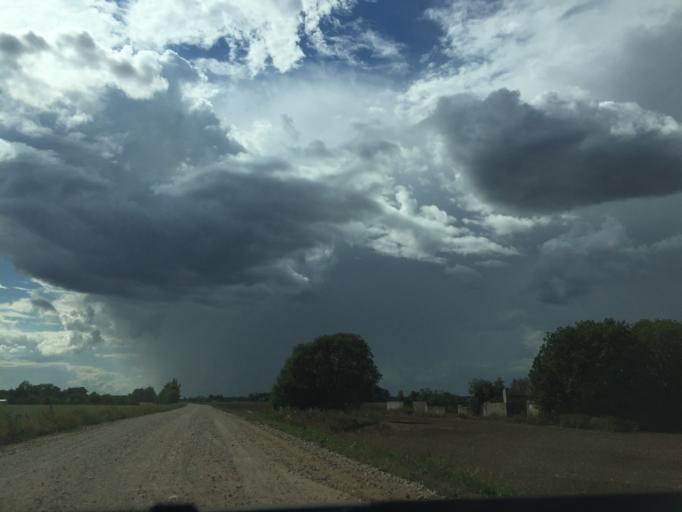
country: LT
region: Siauliu apskritis
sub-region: Joniskis
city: Joniskis
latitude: 56.3739
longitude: 23.5605
